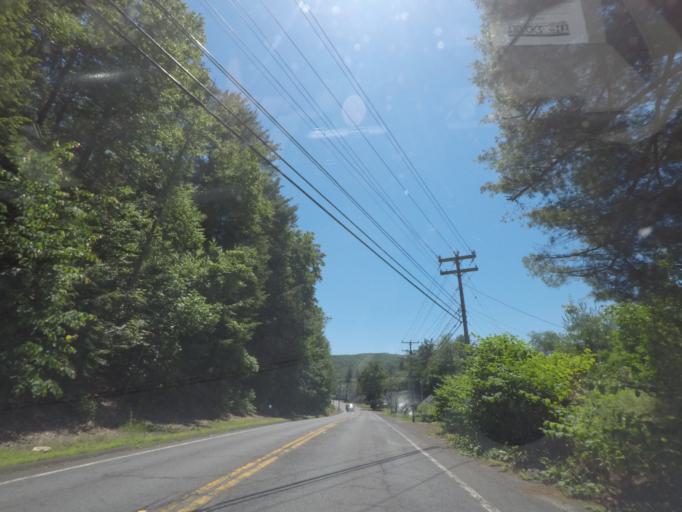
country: US
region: Massachusetts
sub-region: Hampden County
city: Granville
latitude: 42.1960
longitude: -72.8593
